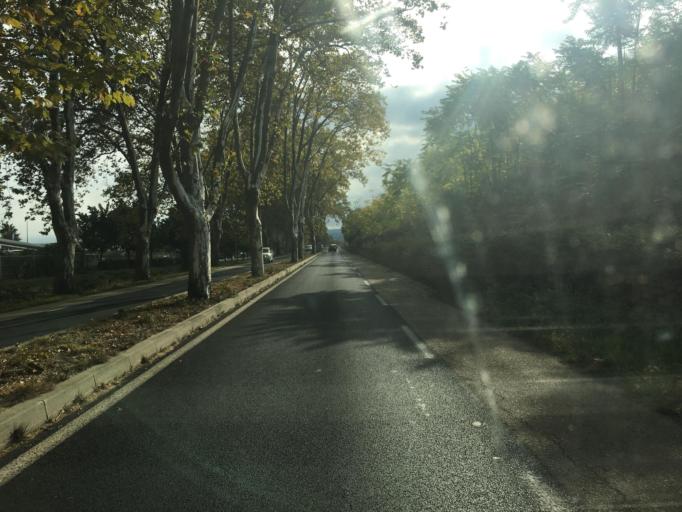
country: FR
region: Languedoc-Roussillon
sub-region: Departement de l'Herault
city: Nebian
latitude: 43.6183
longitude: 3.4468
